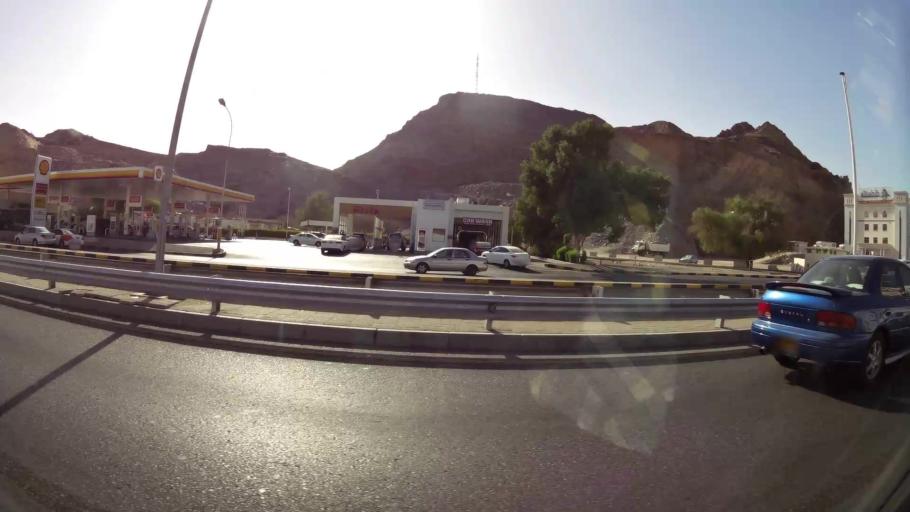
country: OM
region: Muhafazat Masqat
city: Muscat
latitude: 23.5884
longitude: 58.5410
